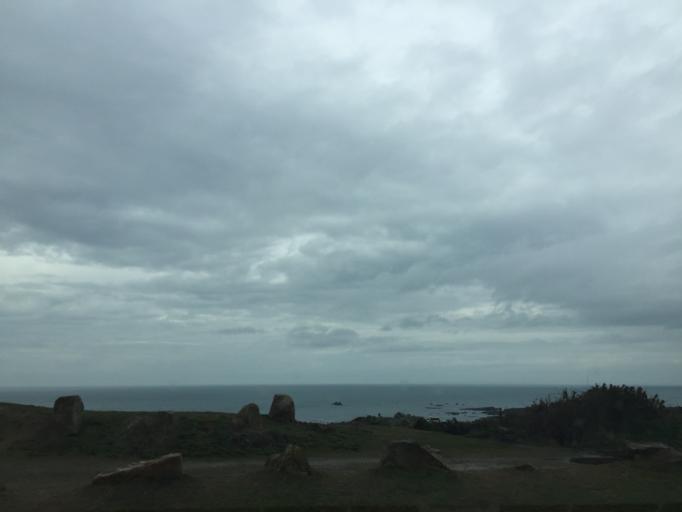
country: JE
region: St Helier
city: Saint Helier
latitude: 49.1800
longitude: -2.2392
